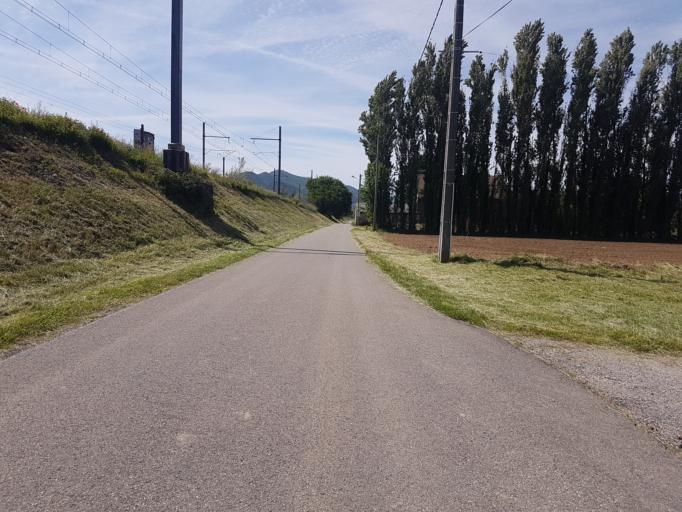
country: FR
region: Rhone-Alpes
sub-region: Departement de l'Ardeche
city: Le Pouzin
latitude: 44.7374
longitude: 4.7475
